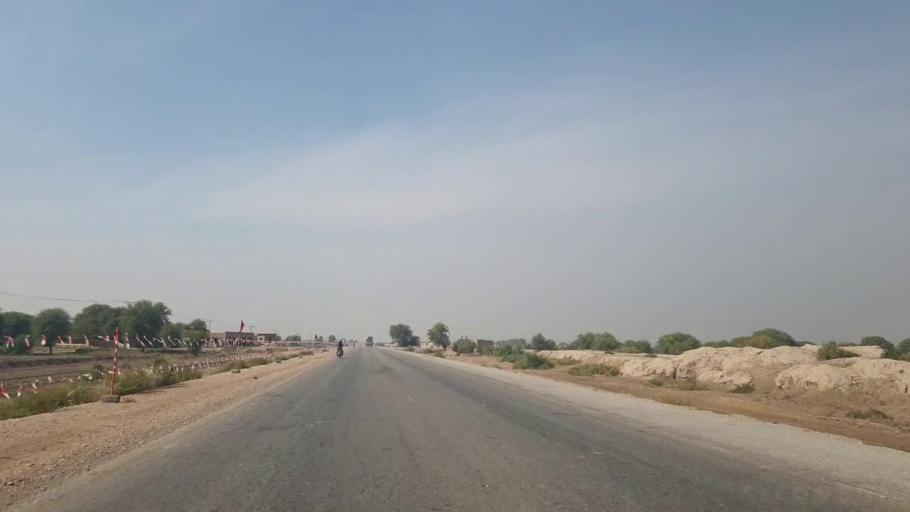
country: PK
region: Sindh
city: Sann
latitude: 25.9888
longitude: 68.1780
